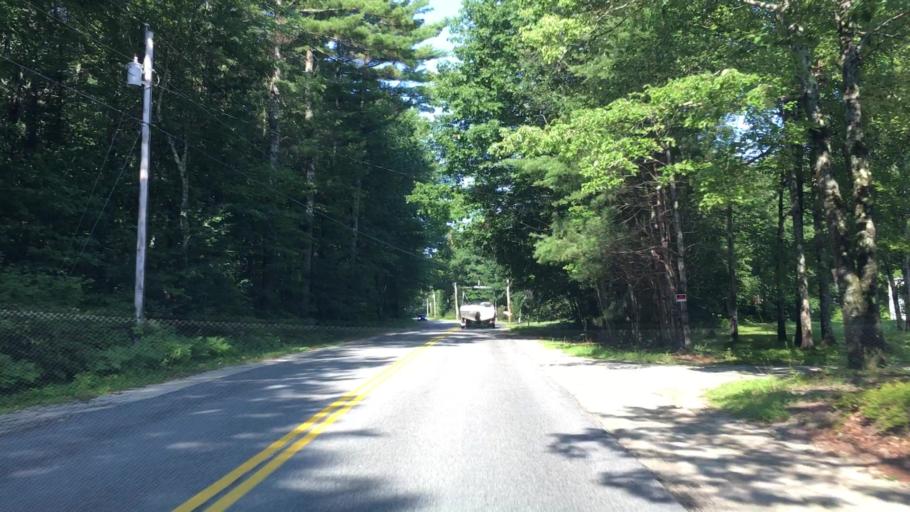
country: US
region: Maine
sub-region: Androscoggin County
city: Minot
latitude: 44.0429
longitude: -70.3368
